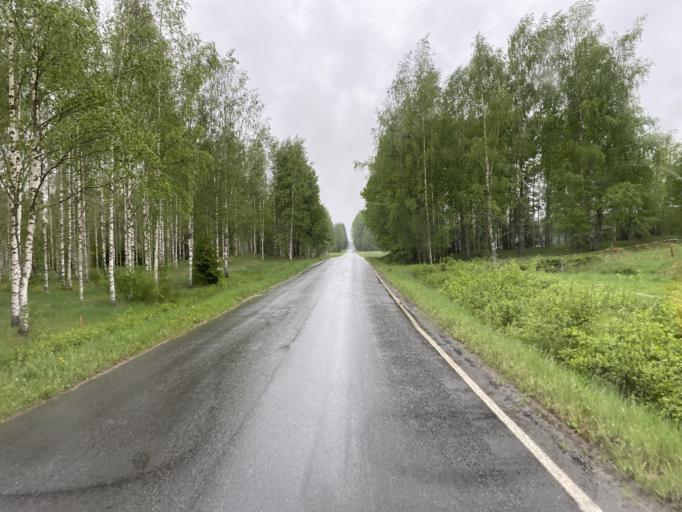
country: FI
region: Haeme
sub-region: Forssa
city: Humppila
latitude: 61.0646
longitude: 23.3237
